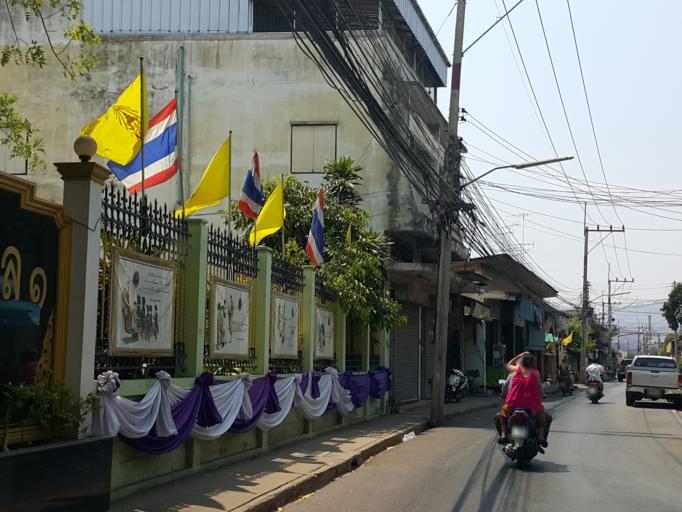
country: TH
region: Kanchanaburi
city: Kanchanaburi
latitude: 14.0272
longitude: 99.5277
